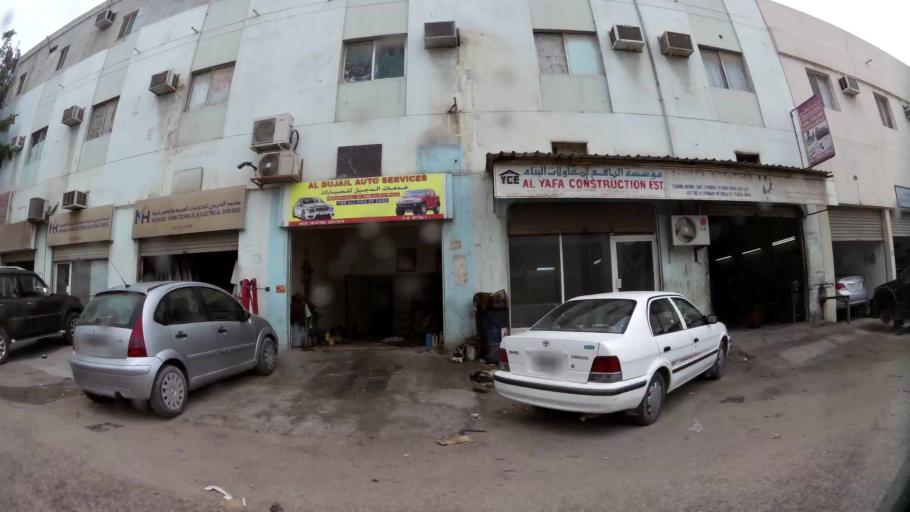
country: BH
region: Northern
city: Madinat `Isa
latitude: 26.1833
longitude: 50.5334
